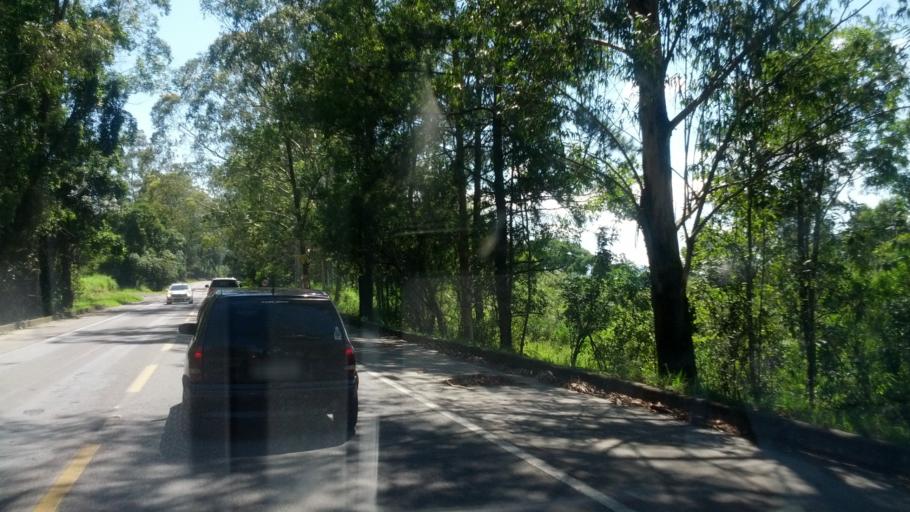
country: BR
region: Santa Catarina
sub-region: Rio Do Sul
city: Rio do Sul
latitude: -27.1705
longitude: -49.5757
